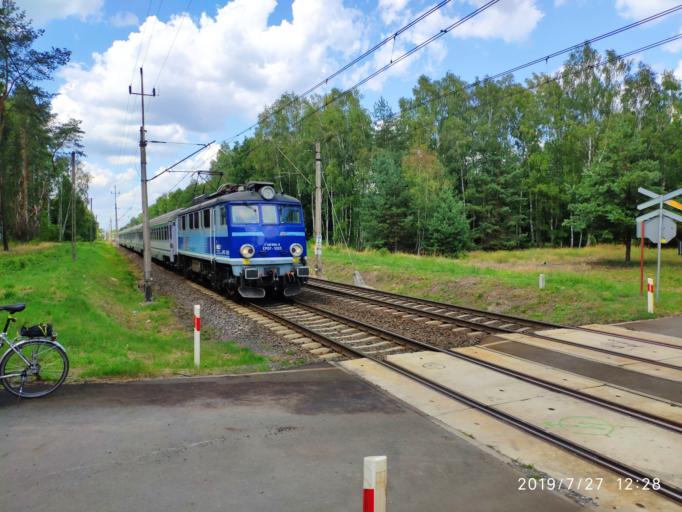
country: PL
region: Lubusz
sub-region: Zielona Gora
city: Zielona Gora
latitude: 51.9413
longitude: 15.5725
